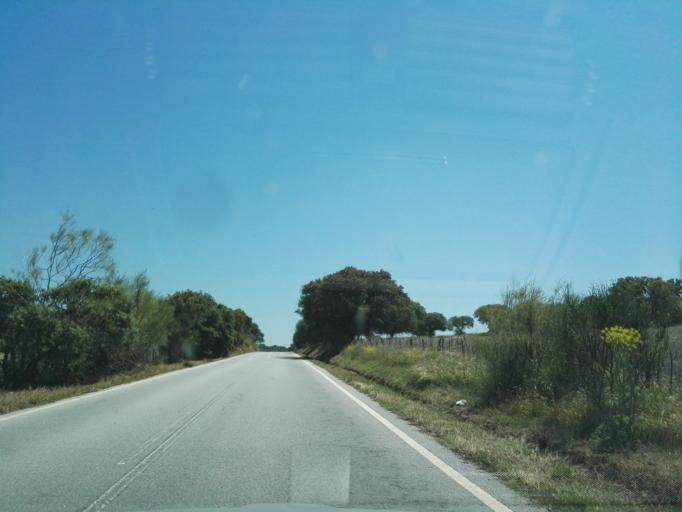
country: PT
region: Portalegre
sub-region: Elvas
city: Elvas
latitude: 38.9979
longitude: -7.1899
